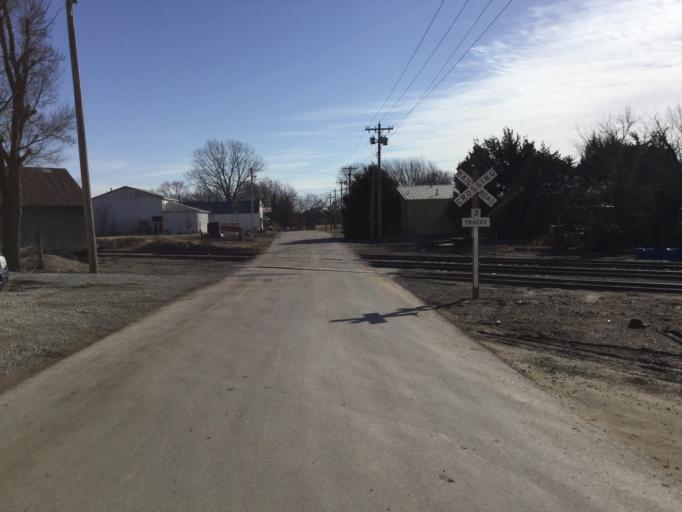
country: US
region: Kansas
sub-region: Douglas County
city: Baldwin City
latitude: 38.7731
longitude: -95.2034
